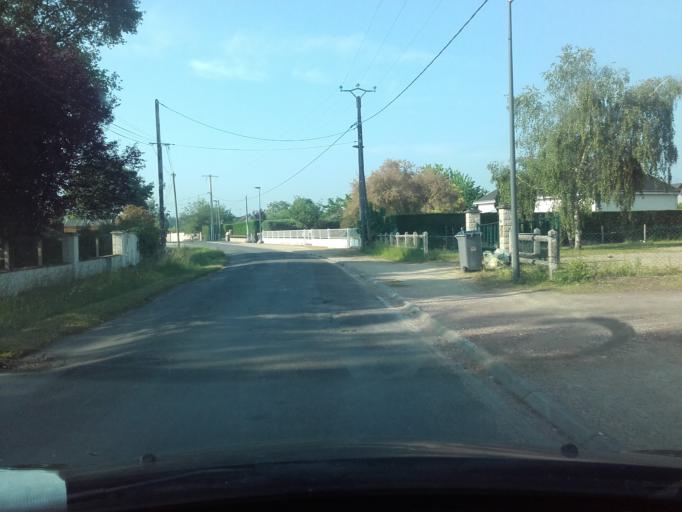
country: FR
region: Centre
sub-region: Departement d'Indre-et-Loire
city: Mazieres-de-Touraine
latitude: 47.3865
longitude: 0.4282
